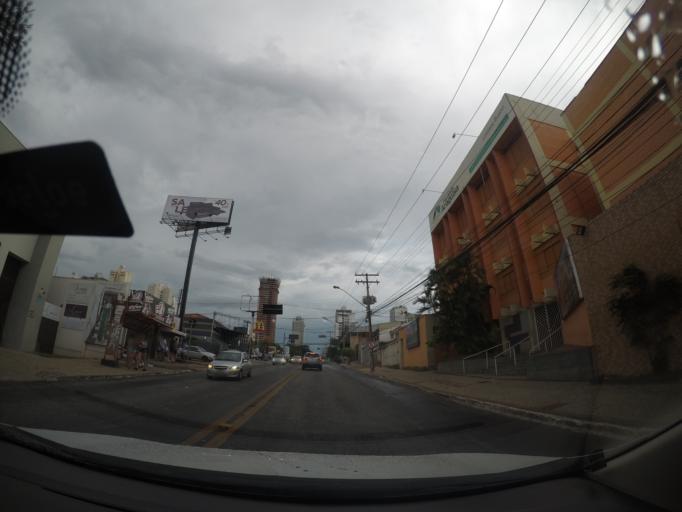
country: BR
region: Goias
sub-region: Goiania
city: Goiania
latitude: -16.7071
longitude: -49.2703
